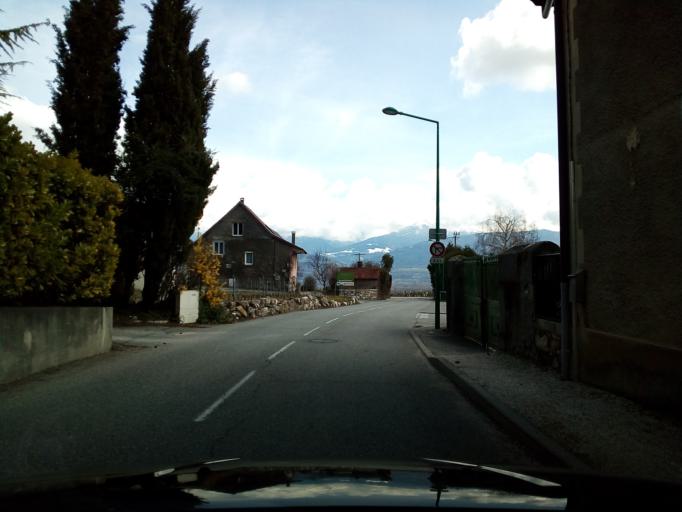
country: FR
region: Rhone-Alpes
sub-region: Departement de la Savoie
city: Les Marches
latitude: 45.4912
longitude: 5.9773
